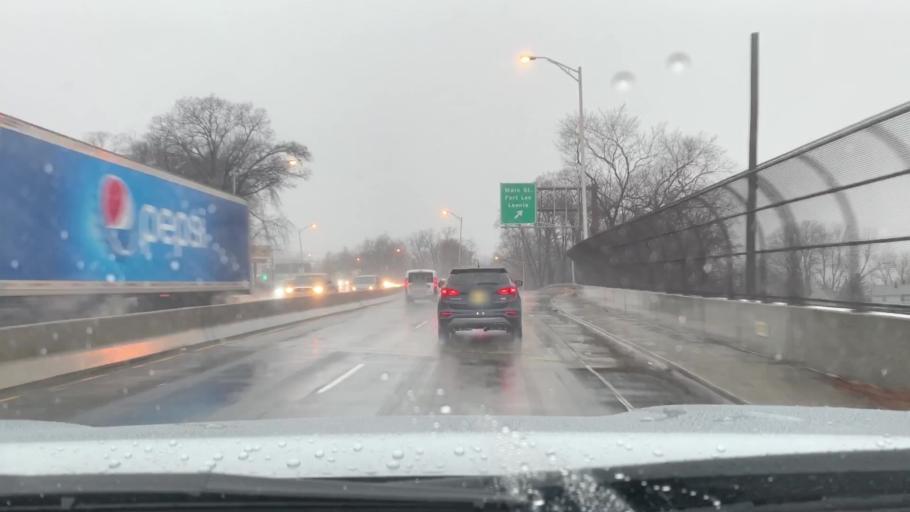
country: US
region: New Jersey
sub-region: Bergen County
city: Leonia
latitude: 40.8585
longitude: -73.9783
